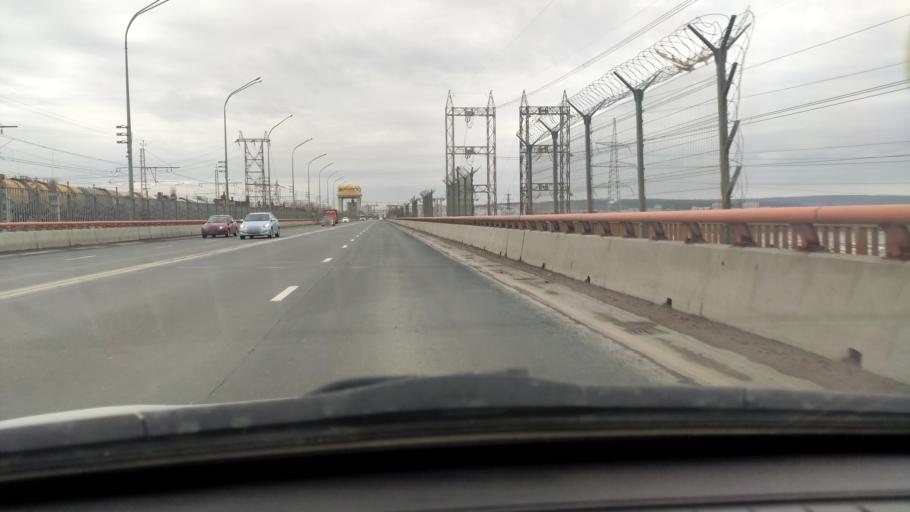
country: RU
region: Samara
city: Zhigulevsk
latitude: 53.4555
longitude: 49.4951
